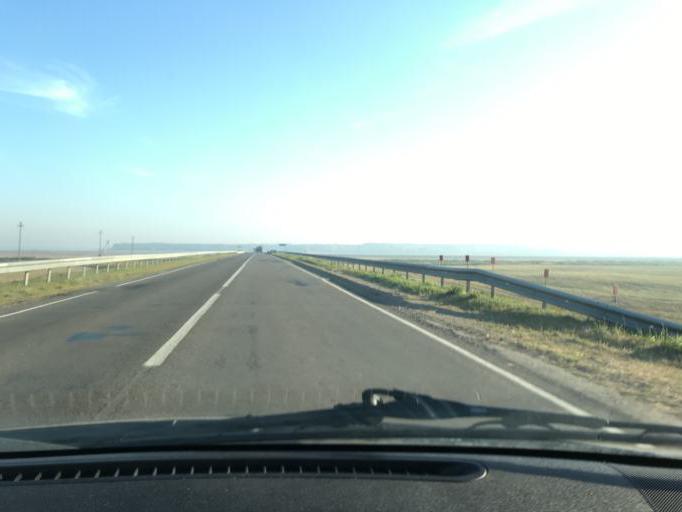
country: BY
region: Brest
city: Asnyezhytsy
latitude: 52.2848
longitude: 26.4089
